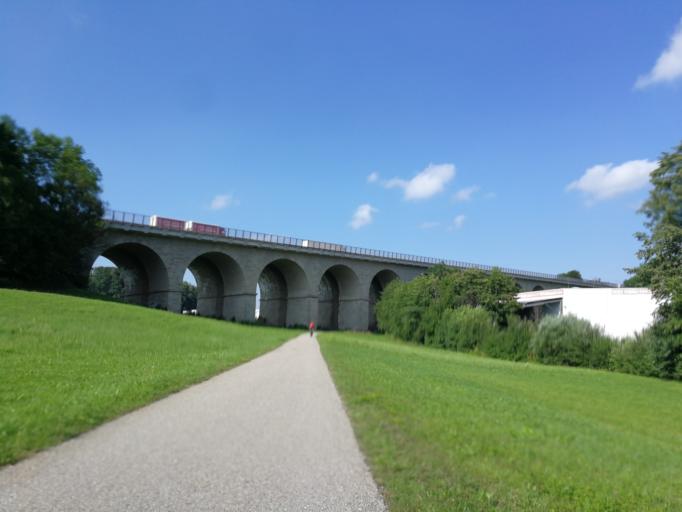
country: AT
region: Salzburg
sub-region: Politischer Bezirk Salzburg-Umgebung
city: Eugendorf
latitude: 47.8512
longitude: 13.1057
